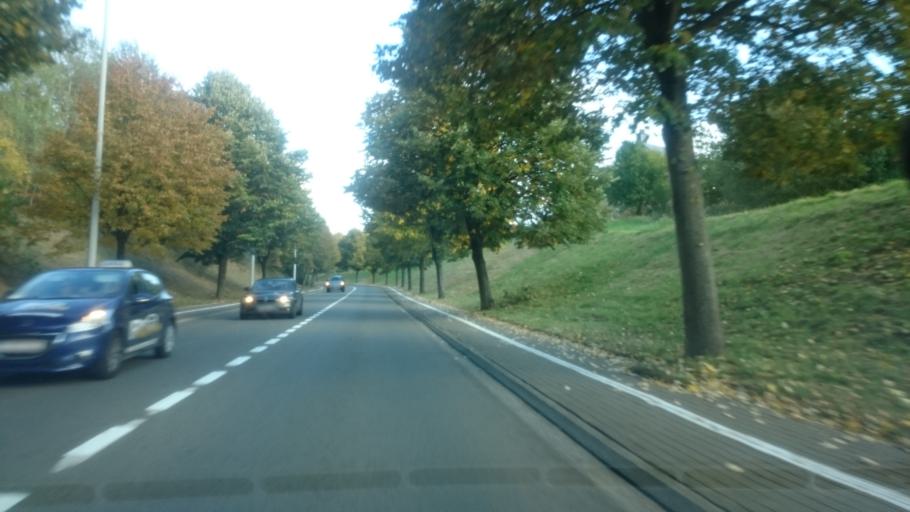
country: BE
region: Wallonia
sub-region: Province du Brabant Wallon
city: Ottignies
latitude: 50.6661
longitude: 4.5858
